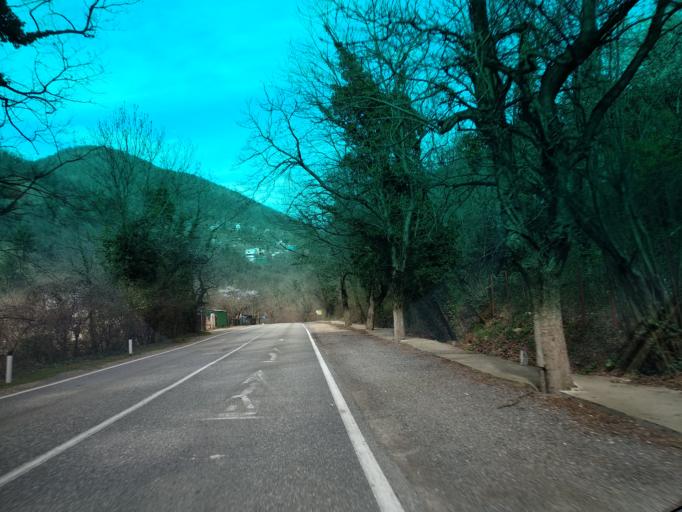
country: RU
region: Krasnodarskiy
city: Tuapse
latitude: 44.0870
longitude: 39.1291
